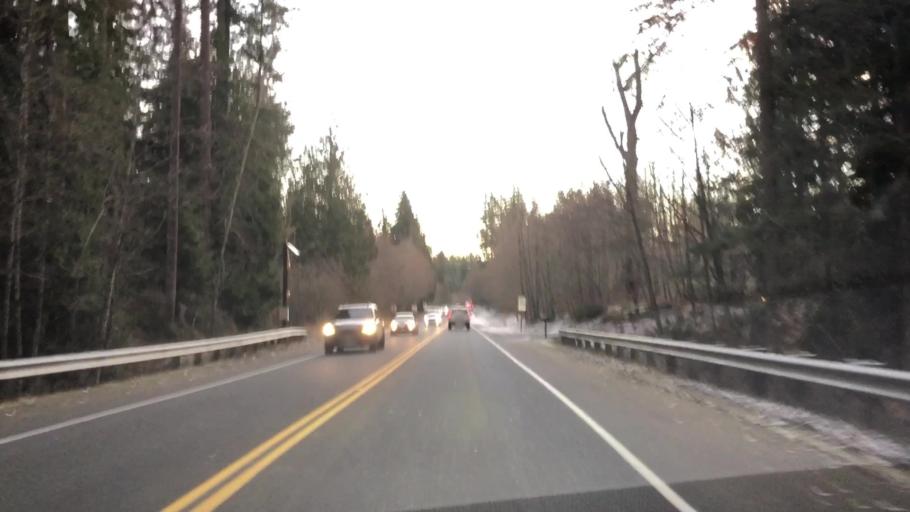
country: US
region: Washington
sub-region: King County
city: Union Hill-Novelty Hill
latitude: 47.7187
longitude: -122.0392
